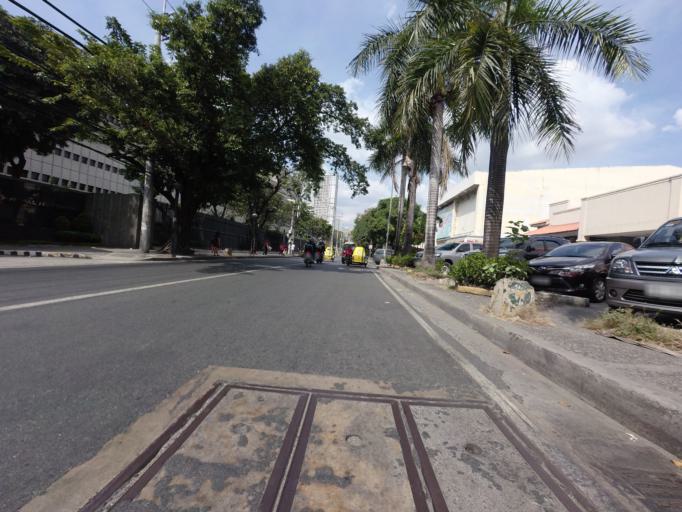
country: PH
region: Metro Manila
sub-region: City of Manila
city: Port Area
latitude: 14.5607
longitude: 120.9892
